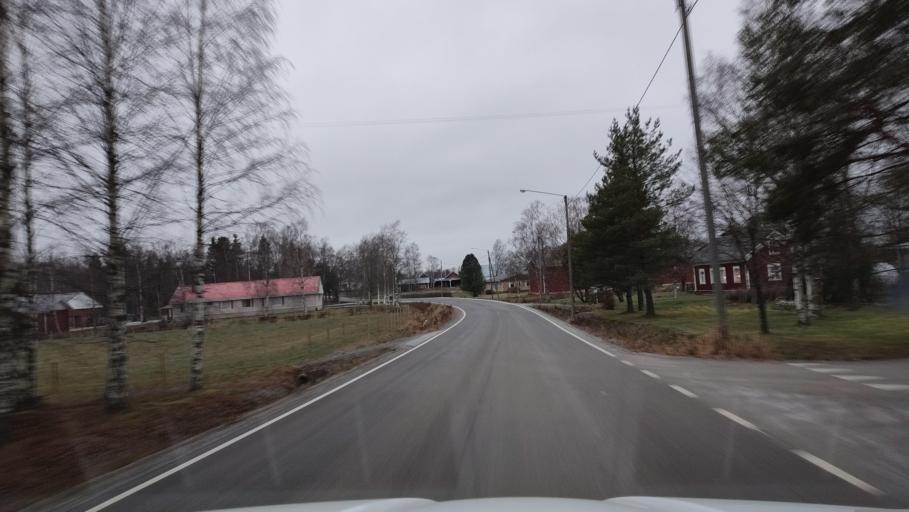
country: FI
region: Ostrobothnia
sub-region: Sydosterbotten
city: Kristinestad
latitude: 62.2487
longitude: 21.5361
